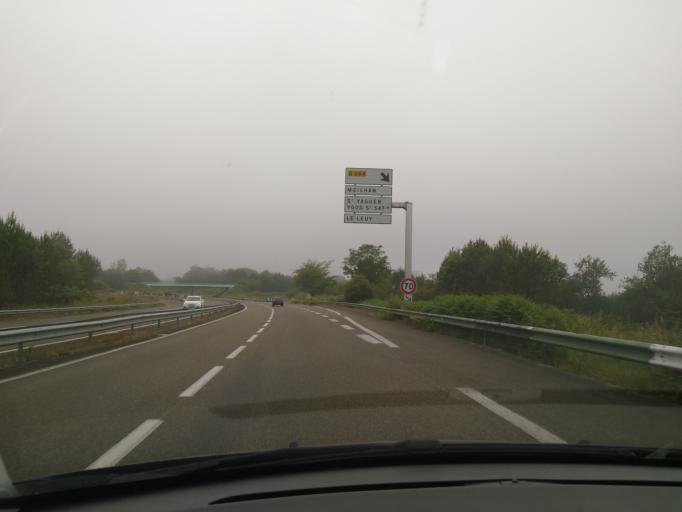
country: FR
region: Aquitaine
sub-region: Departement des Landes
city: Meilhan
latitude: 43.8638
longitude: -0.6896
